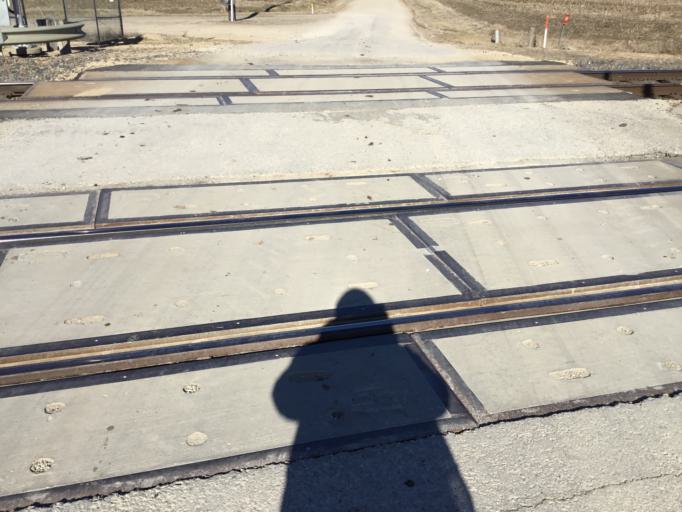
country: US
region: Kansas
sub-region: Douglas County
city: Lawrence
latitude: 38.9837
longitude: -95.2052
